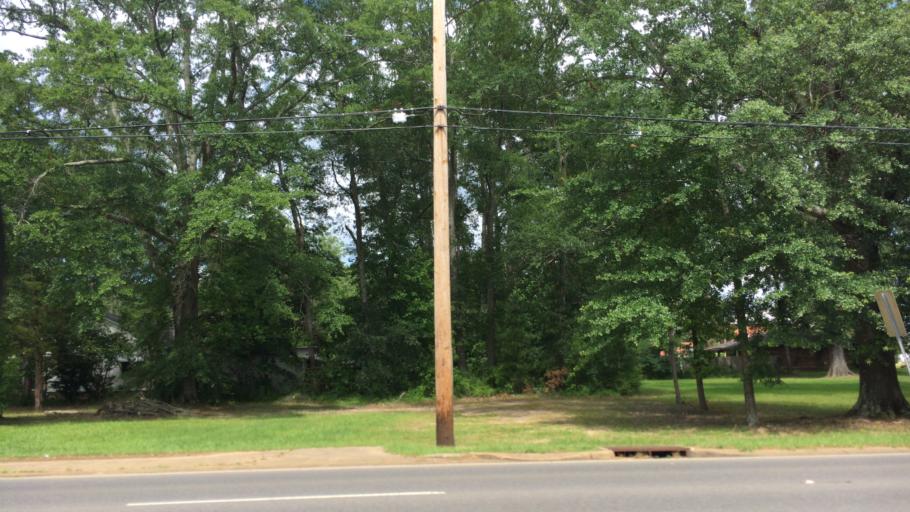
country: US
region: Louisiana
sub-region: Lincoln Parish
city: Ruston
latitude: 32.5117
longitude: -92.6380
